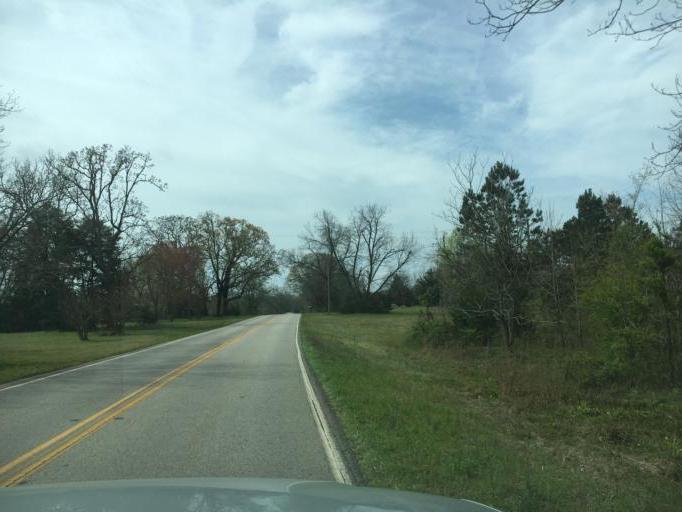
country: US
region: Georgia
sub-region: Hart County
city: Royston
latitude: 34.3261
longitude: -83.0404
